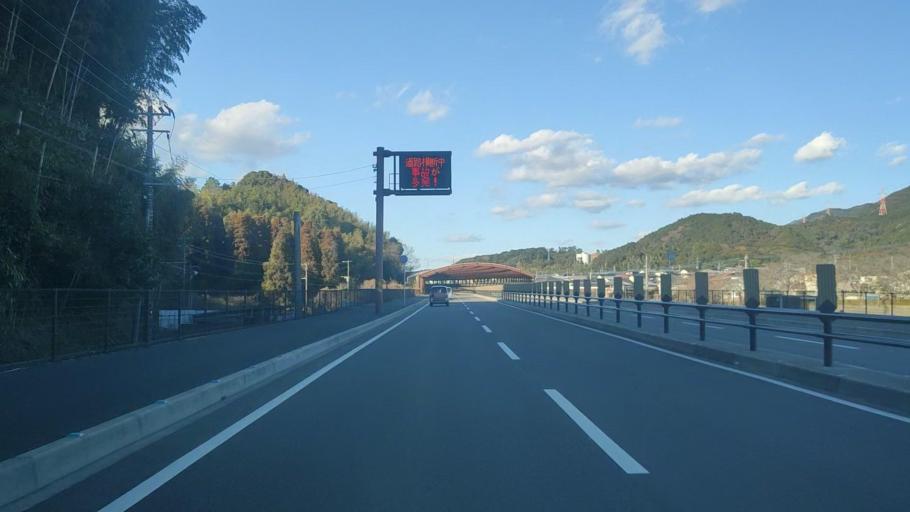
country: JP
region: Fukuoka
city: Dazaifu
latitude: 33.5083
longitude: 130.5503
